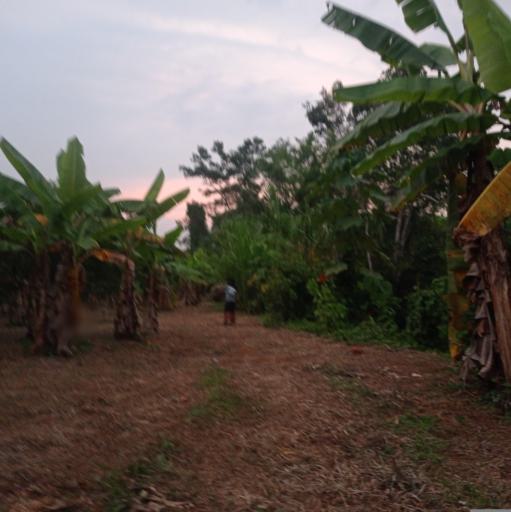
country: BO
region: La Paz
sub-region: Provincia Larecaja
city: Guanay
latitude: -15.5678
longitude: -67.3284
